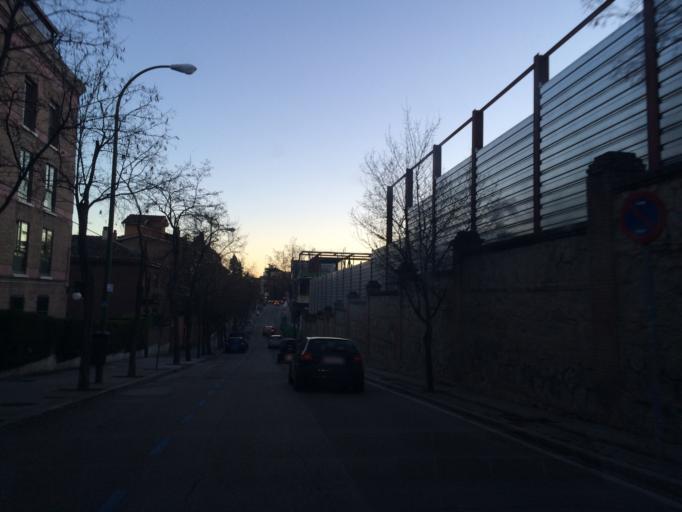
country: ES
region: Madrid
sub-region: Provincia de Madrid
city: Chamartin
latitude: 40.4697
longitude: -3.6822
